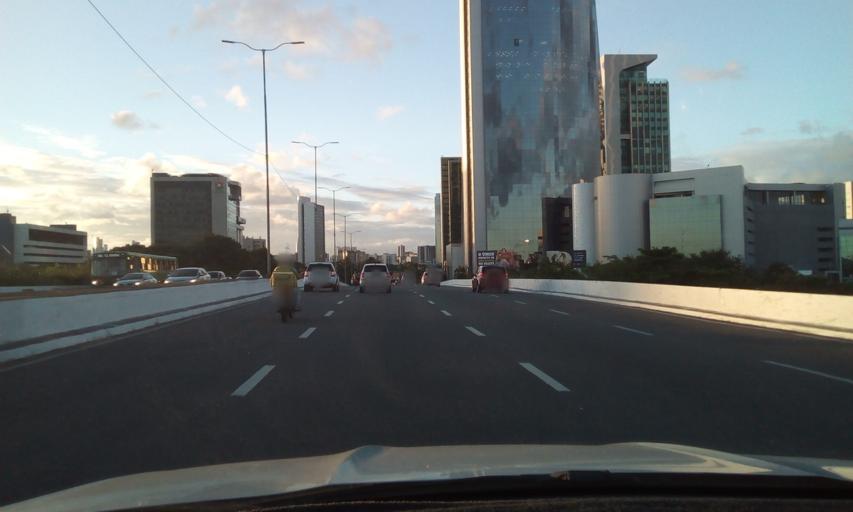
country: BR
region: Pernambuco
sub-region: Recife
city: Recife
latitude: -8.0676
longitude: -34.8968
